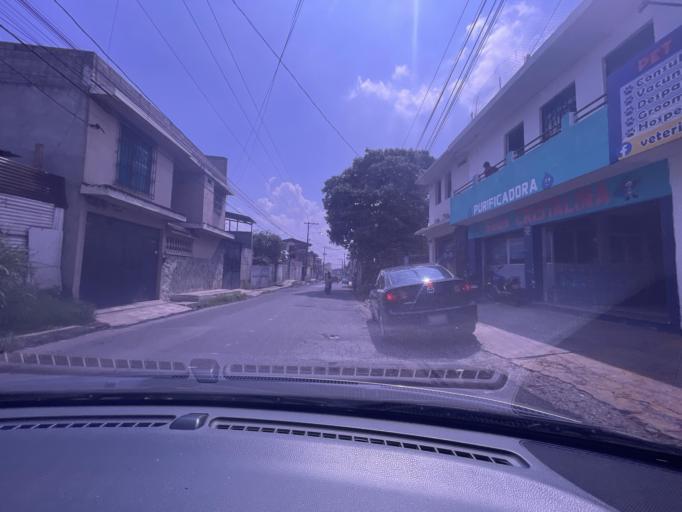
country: GT
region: Guatemala
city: Guatemala City
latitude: 14.6728
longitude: -90.5462
